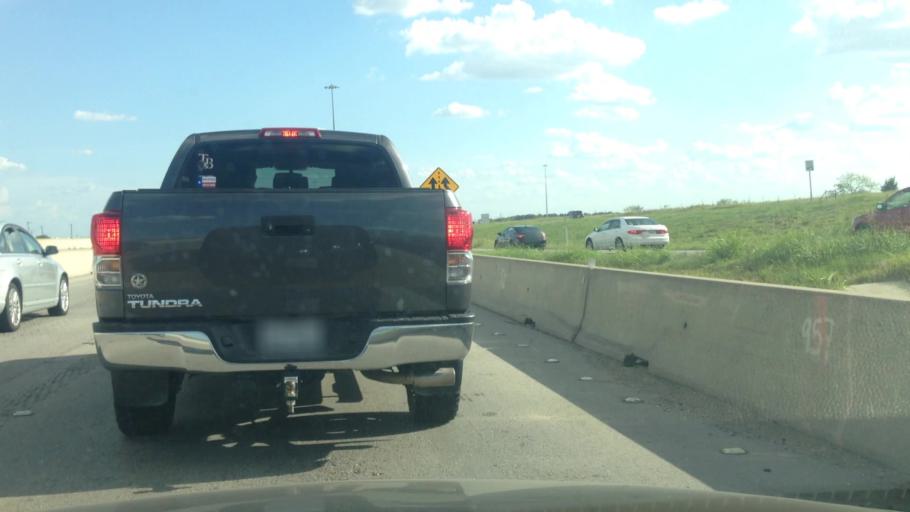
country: US
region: Texas
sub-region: Tarrant County
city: Blue Mound
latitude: 32.8959
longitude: -97.3175
